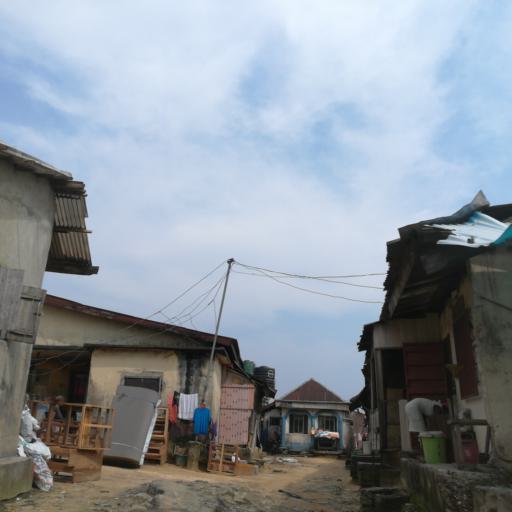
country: NG
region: Rivers
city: Port Harcourt
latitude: 4.8637
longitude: 7.0222
